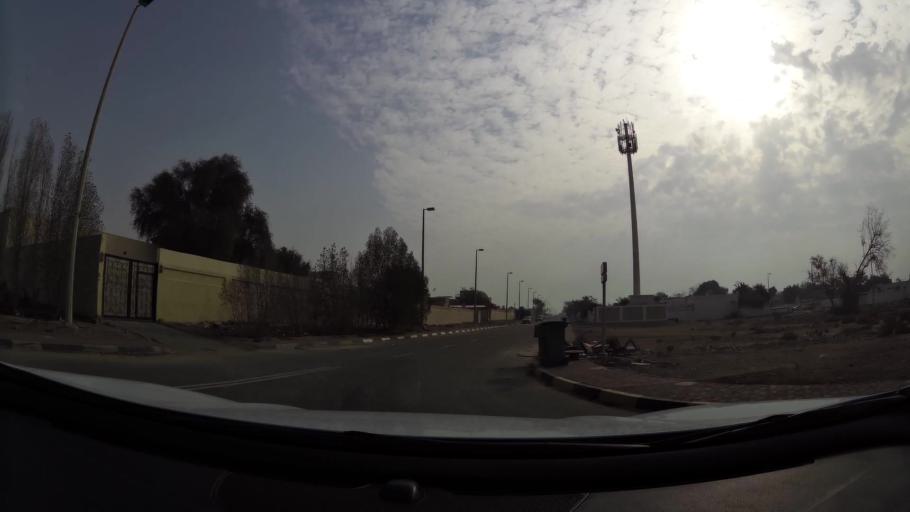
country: AE
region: Abu Dhabi
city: Abu Dhabi
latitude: 24.6800
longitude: 54.7721
